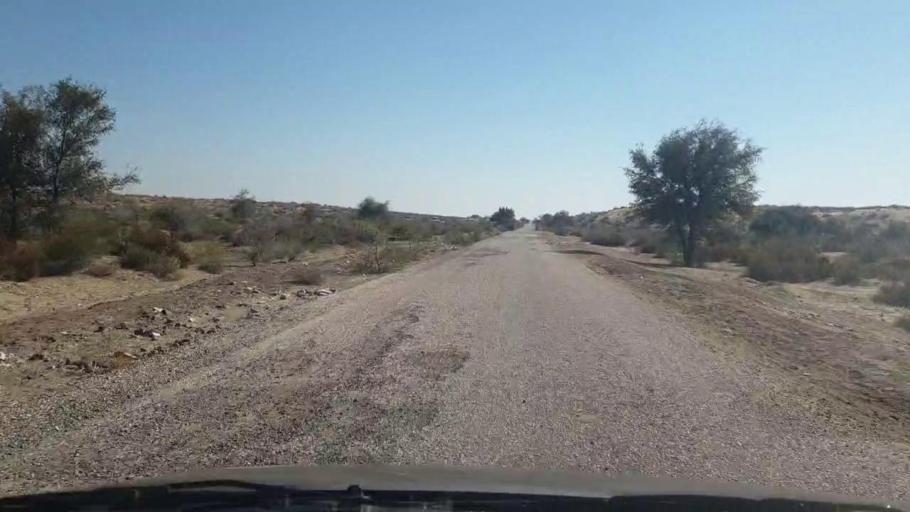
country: PK
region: Sindh
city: Bozdar
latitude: 27.0386
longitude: 68.6924
